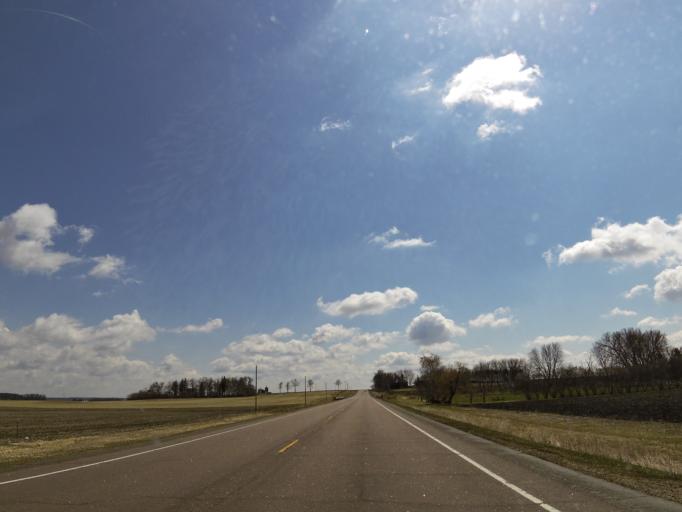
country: US
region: Minnesota
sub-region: Goodhue County
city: Cannon Falls
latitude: 44.5601
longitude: -92.9949
